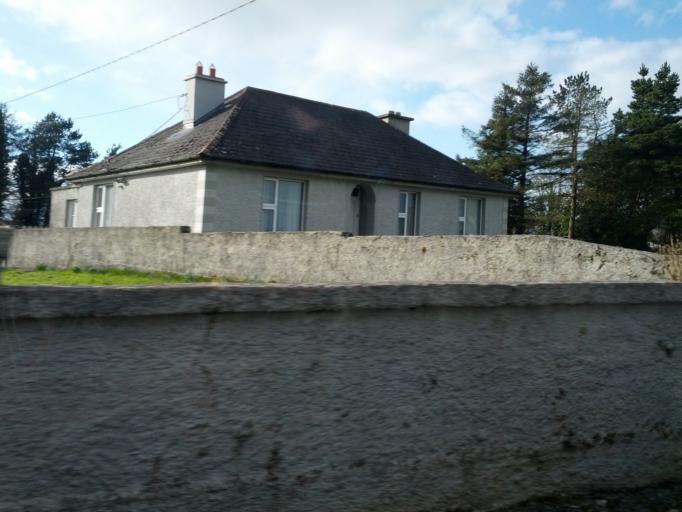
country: IE
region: Connaught
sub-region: County Galway
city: Athenry
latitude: 53.4505
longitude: -8.6424
